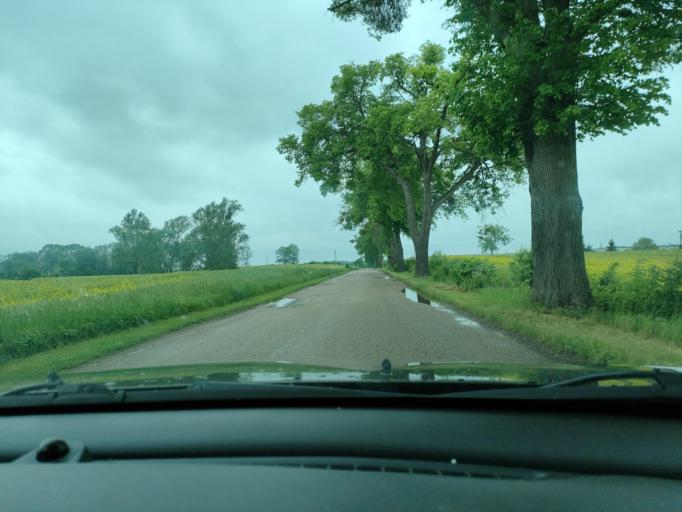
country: PL
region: Pomeranian Voivodeship
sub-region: Powiat kwidzynski
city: Gardeja
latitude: 53.5691
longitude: 19.0011
